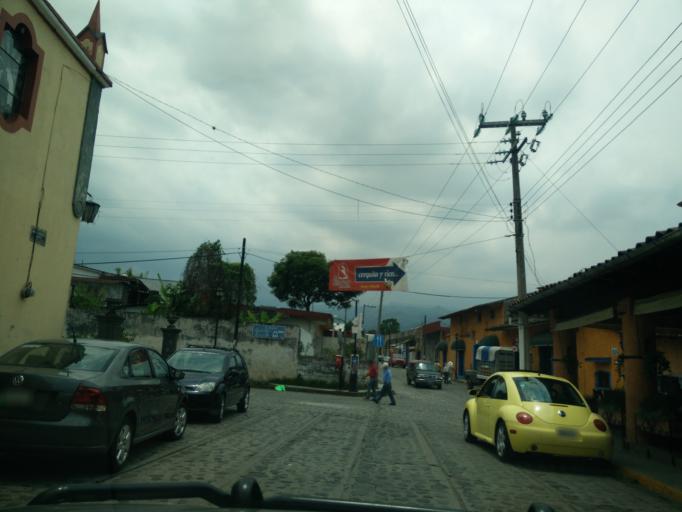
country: MX
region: Veracruz
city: Xico
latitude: 19.4184
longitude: -97.0022
